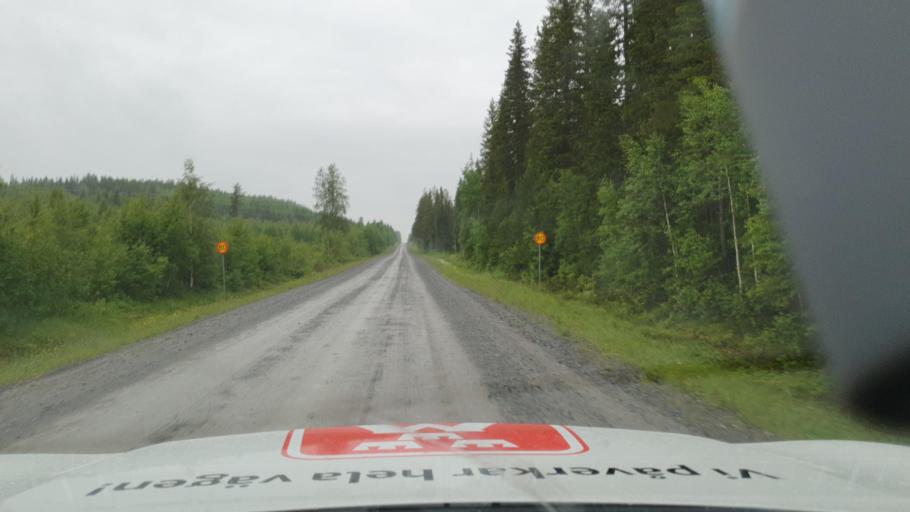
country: SE
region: Vaesterbotten
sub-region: Bjurholms Kommun
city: Bjurholm
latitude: 63.8519
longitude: 19.4745
